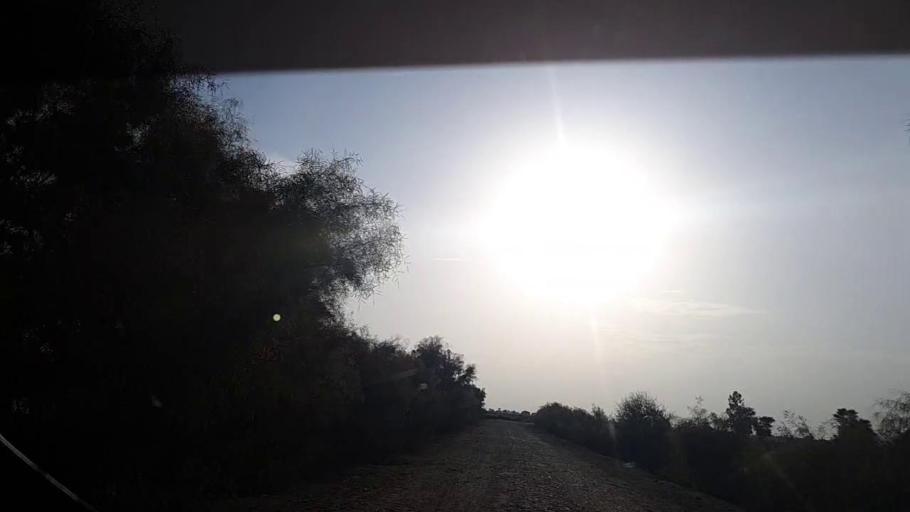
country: PK
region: Sindh
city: Khanpur
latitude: 27.8082
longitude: 69.3260
